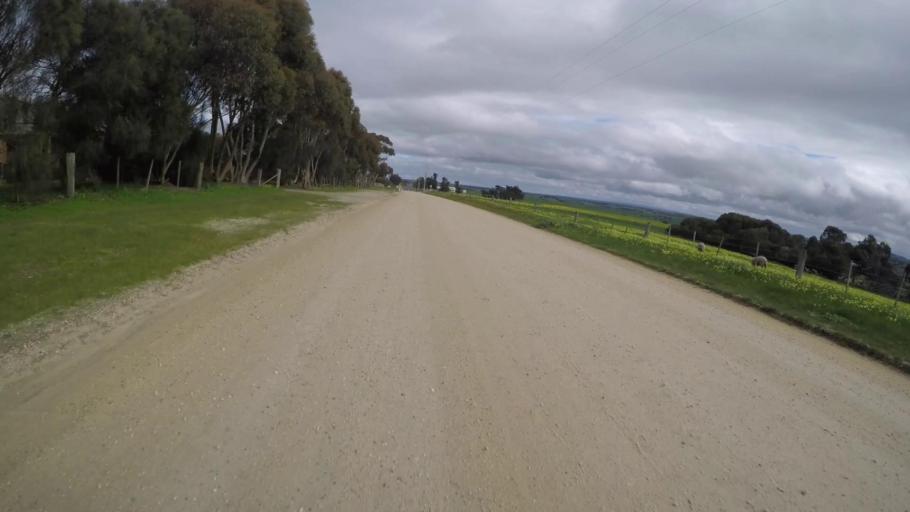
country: AU
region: Victoria
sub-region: Greater Geelong
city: Wandana Heights
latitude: -38.1683
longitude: 144.2726
